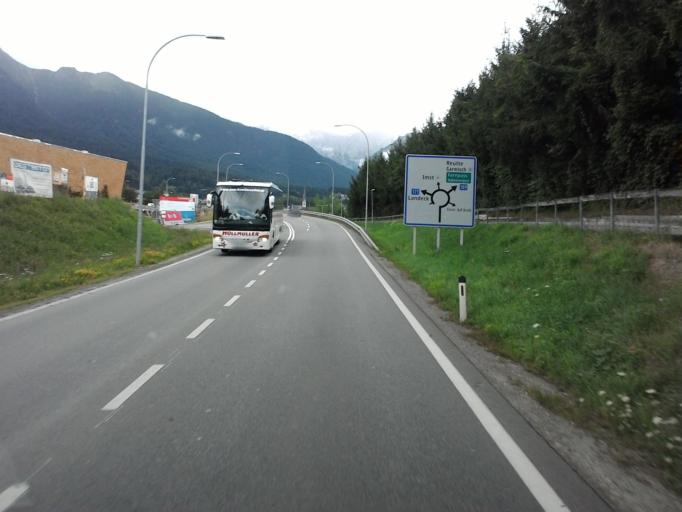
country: AT
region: Tyrol
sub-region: Politischer Bezirk Imst
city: Imst
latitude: 47.2328
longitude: 10.7445
